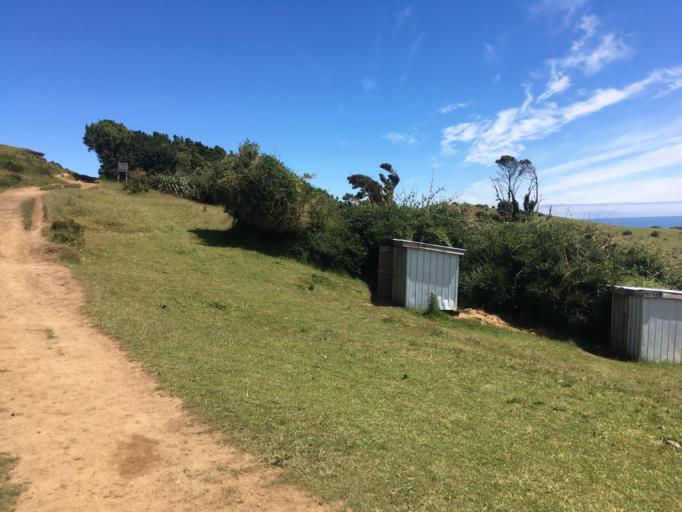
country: CL
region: Los Lagos
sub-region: Provincia de Chiloe
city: Chonchi
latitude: -42.7127
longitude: -74.1430
